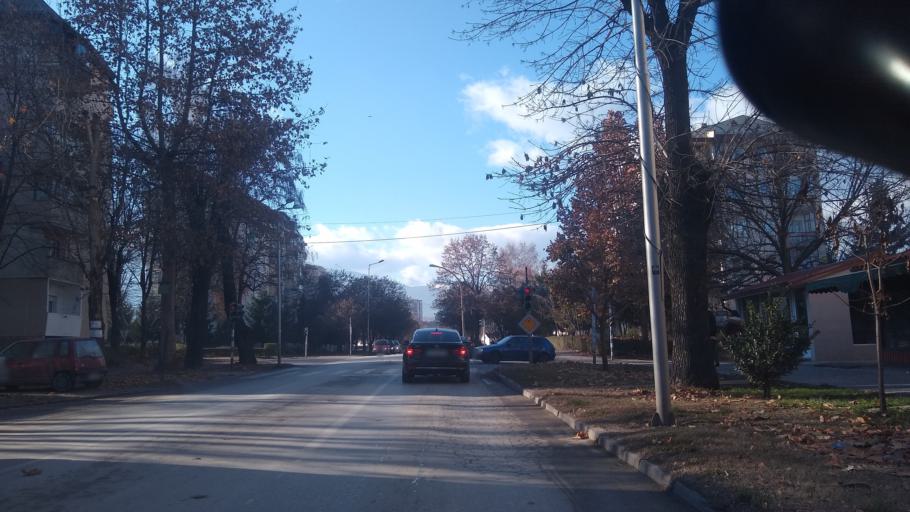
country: MK
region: Bitola
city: Bitola
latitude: 41.0238
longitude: 21.3247
